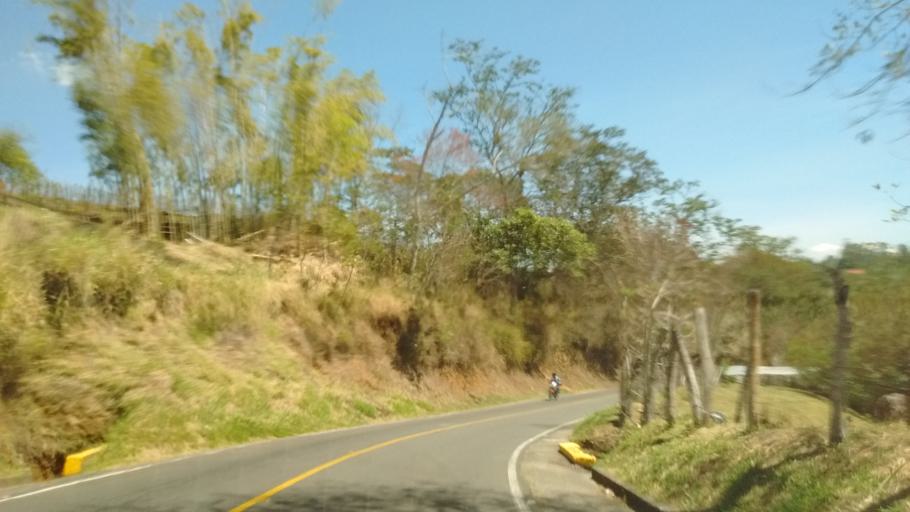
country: CO
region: Cauca
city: Popayan
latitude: 2.3602
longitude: -76.6846
